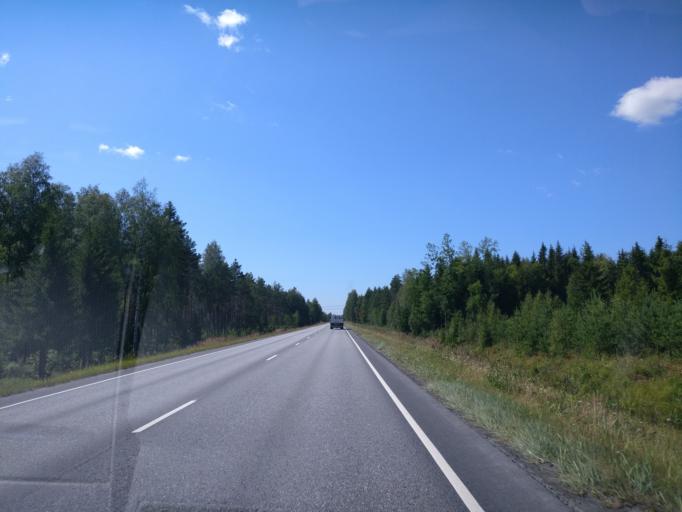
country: FI
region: Satakunta
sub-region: Pori
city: Kullaa
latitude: 61.4592
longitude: 22.0846
